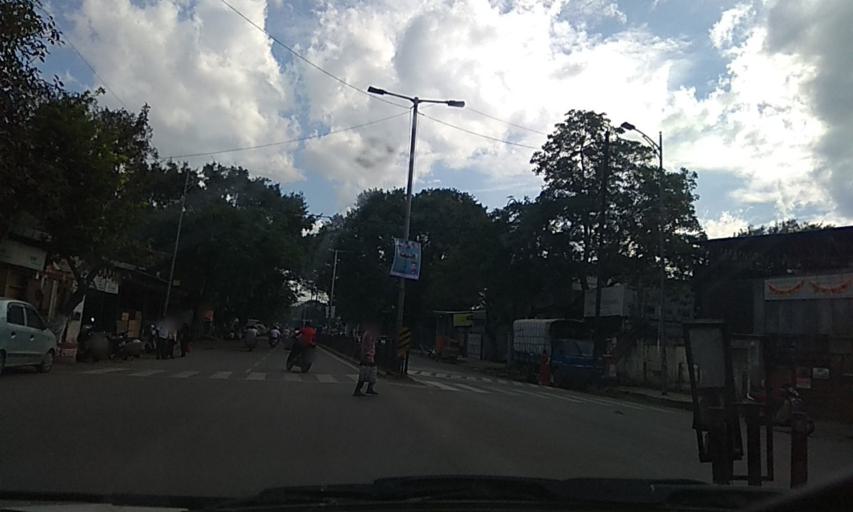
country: IN
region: Maharashtra
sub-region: Pune Division
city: Pune
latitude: 18.5098
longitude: 73.8682
